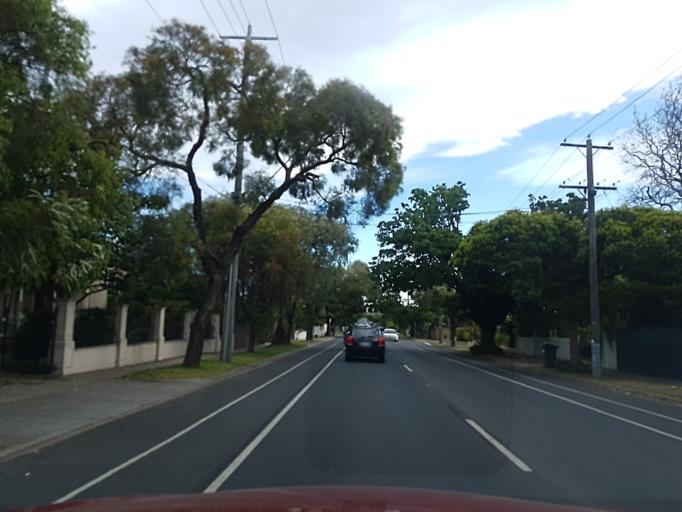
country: AU
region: Victoria
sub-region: Glen Eira
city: Caulfield
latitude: -37.8872
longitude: 145.0148
